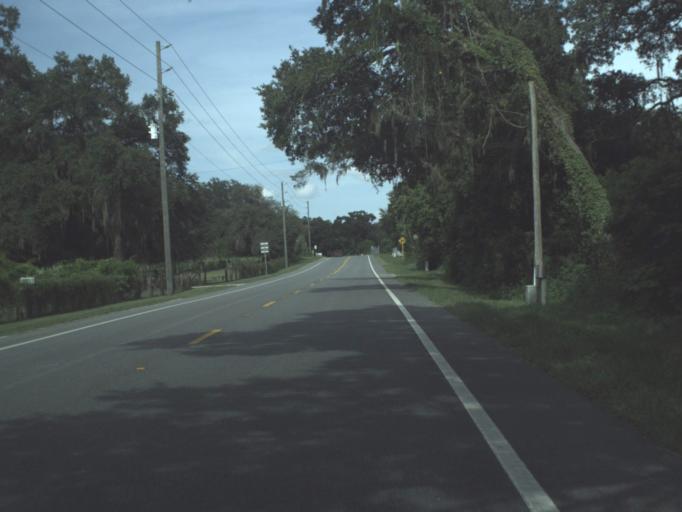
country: US
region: Florida
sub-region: Pasco County
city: Lacoochee
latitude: 28.4652
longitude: -82.1747
